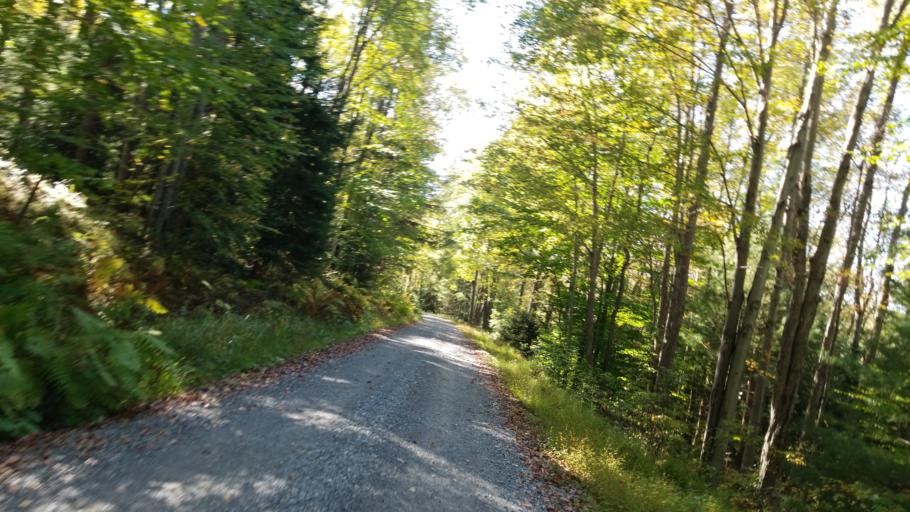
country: US
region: Pennsylvania
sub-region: Clearfield County
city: Clearfield
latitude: 41.1868
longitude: -78.5093
